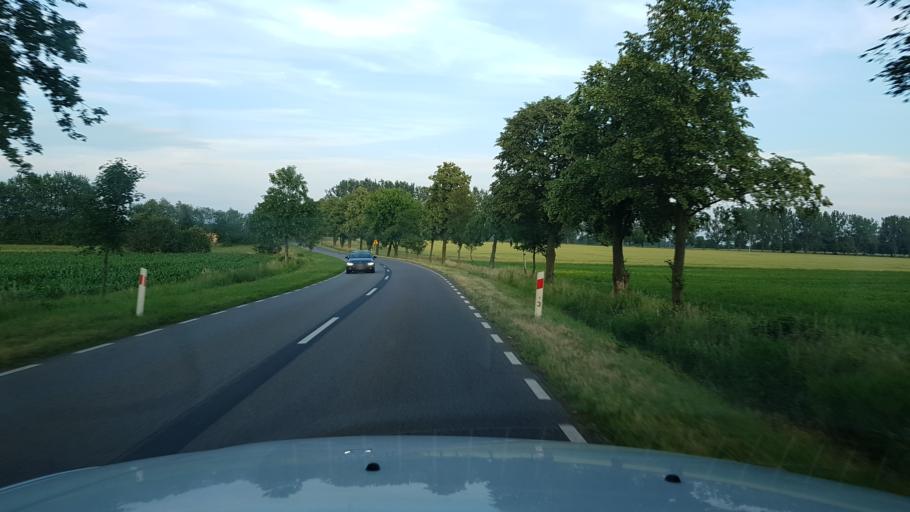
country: PL
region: West Pomeranian Voivodeship
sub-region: Powiat goleniowski
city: Nowogard
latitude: 53.6526
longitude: 15.2019
